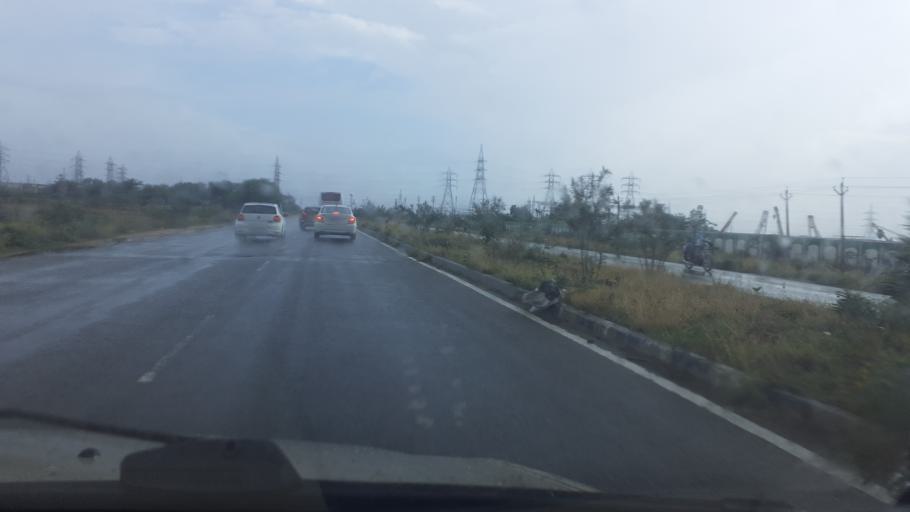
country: IN
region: Tamil Nadu
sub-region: Tirunelveli Kattabo
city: Gangaikondan
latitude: 8.8922
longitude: 77.7671
